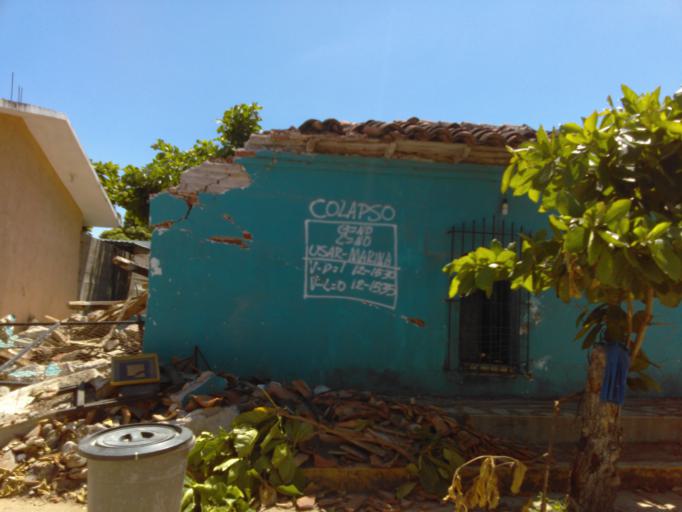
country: MX
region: Oaxaca
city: Asuncion Ixtaltepec
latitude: 16.5051
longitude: -95.0582
